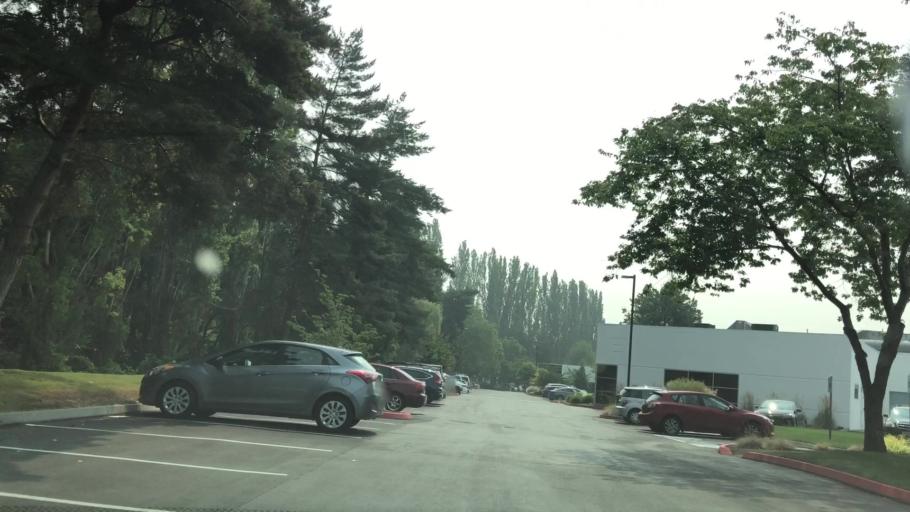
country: US
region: Washington
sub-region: King County
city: Woodinville
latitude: 47.7653
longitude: -122.1816
